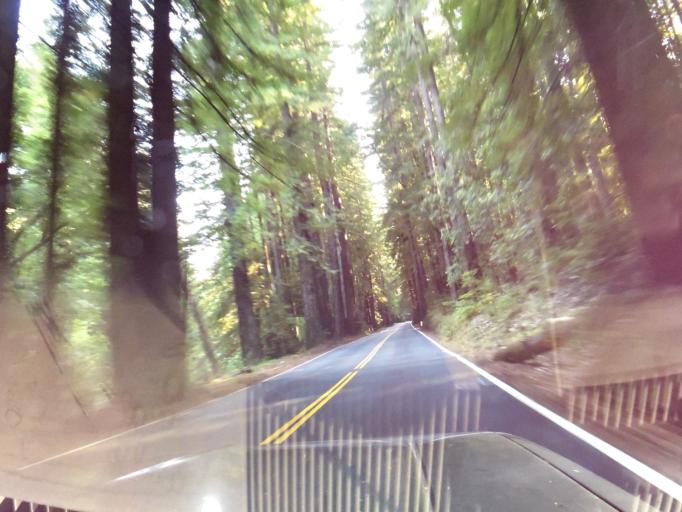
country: US
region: California
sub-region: Mendocino County
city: Boonville
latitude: 39.1586
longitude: -123.6040
